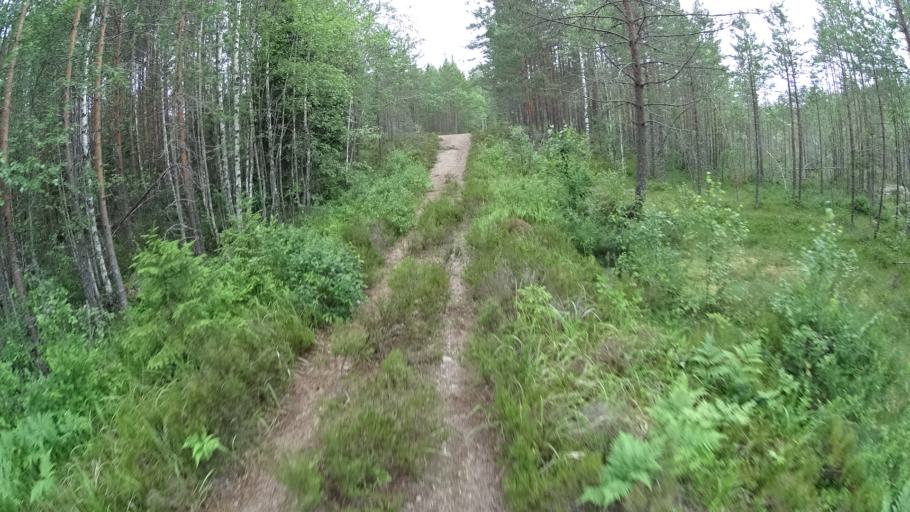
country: FI
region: Southern Savonia
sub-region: Mikkeli
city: Maentyharju
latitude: 61.1843
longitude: 26.8931
